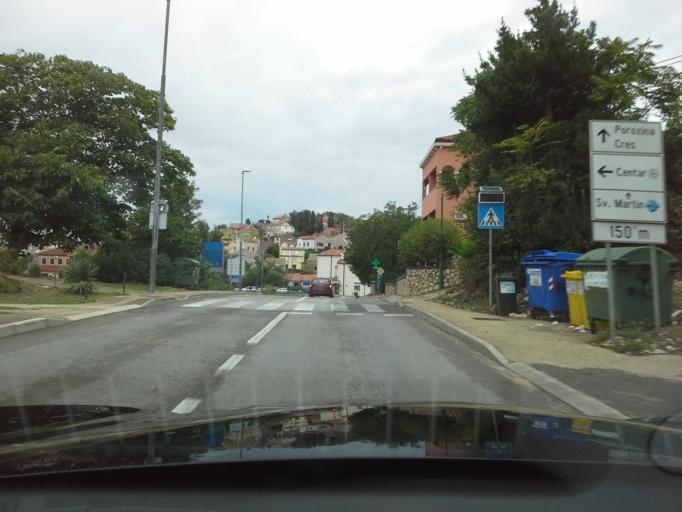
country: HR
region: Primorsko-Goranska
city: Mali Losinj
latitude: 44.5284
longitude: 14.4772
